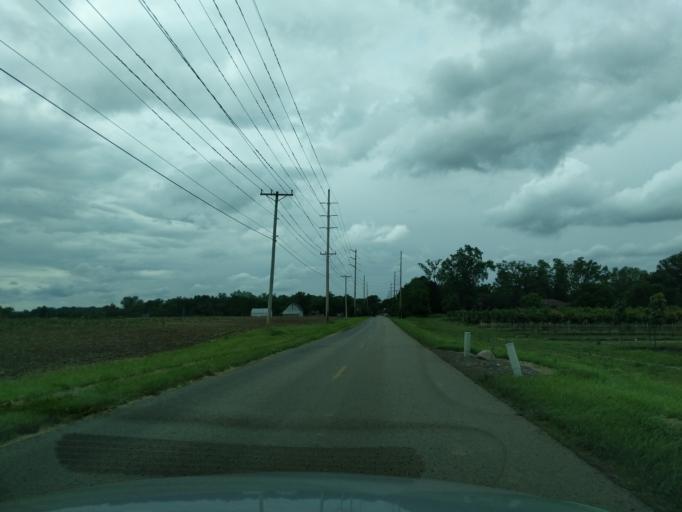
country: US
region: Indiana
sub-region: Madison County
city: Edgewood
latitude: 40.0576
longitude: -85.7302
